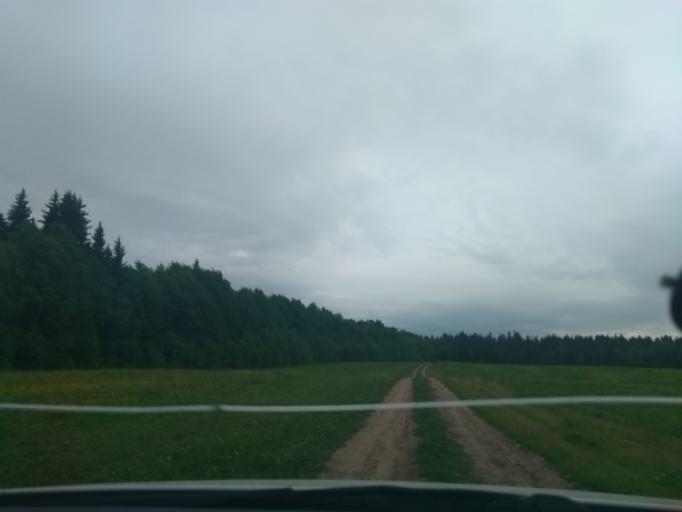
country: RU
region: Perm
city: Perm
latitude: 57.9876
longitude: 56.3349
